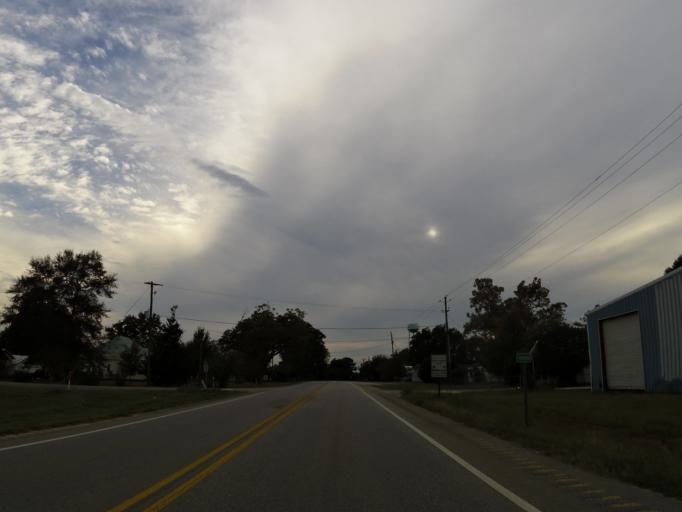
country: US
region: Alabama
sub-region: Monroe County
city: Frisco City
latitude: 31.3077
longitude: -87.4944
